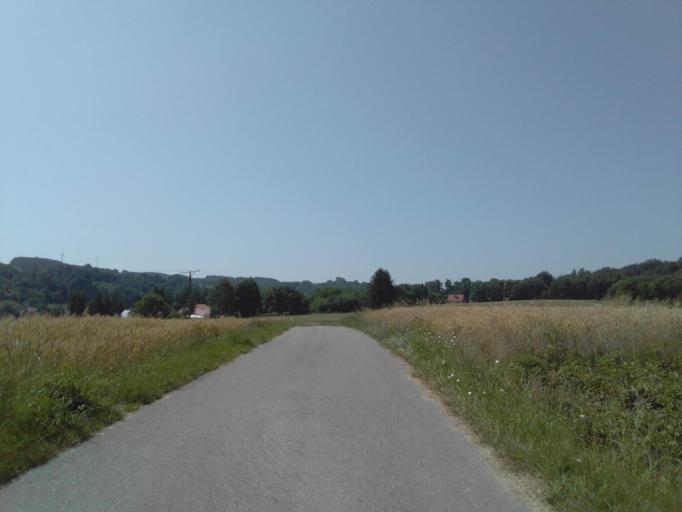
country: PL
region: Subcarpathian Voivodeship
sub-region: Powiat ropczycko-sedziszowski
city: Zagorzyce
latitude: 50.0380
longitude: 21.6518
